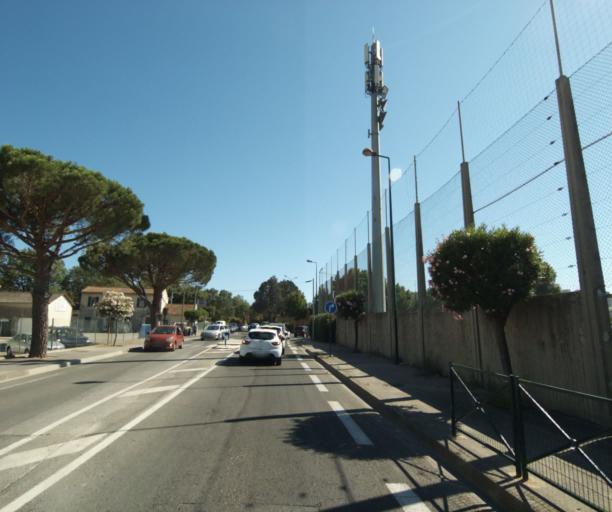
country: FR
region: Provence-Alpes-Cote d'Azur
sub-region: Departement du Var
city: La Garde
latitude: 43.1208
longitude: 6.0118
